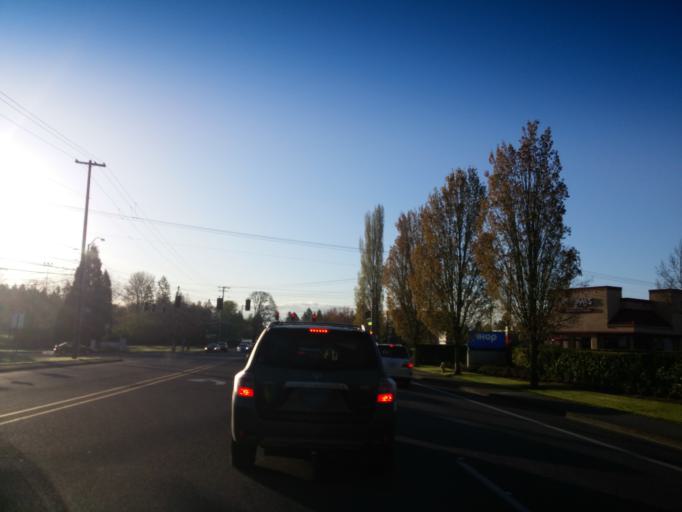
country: US
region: Oregon
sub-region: Washington County
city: Oak Hills
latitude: 45.5171
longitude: -122.8406
